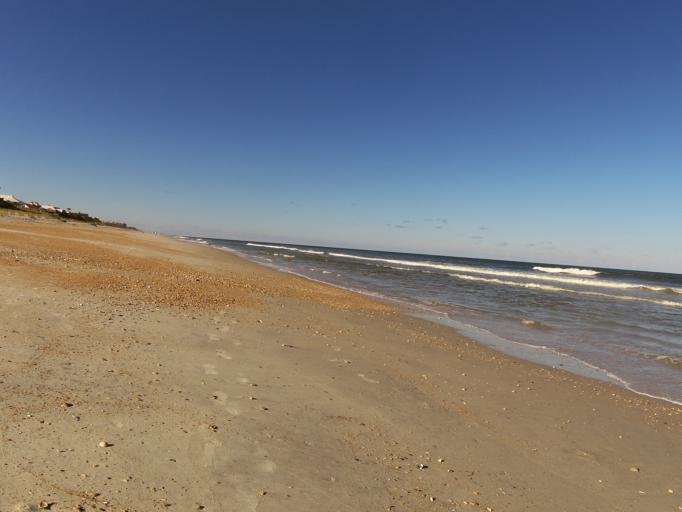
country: US
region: Florida
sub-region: Saint Johns County
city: Sawgrass
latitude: 30.1855
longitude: -81.3617
